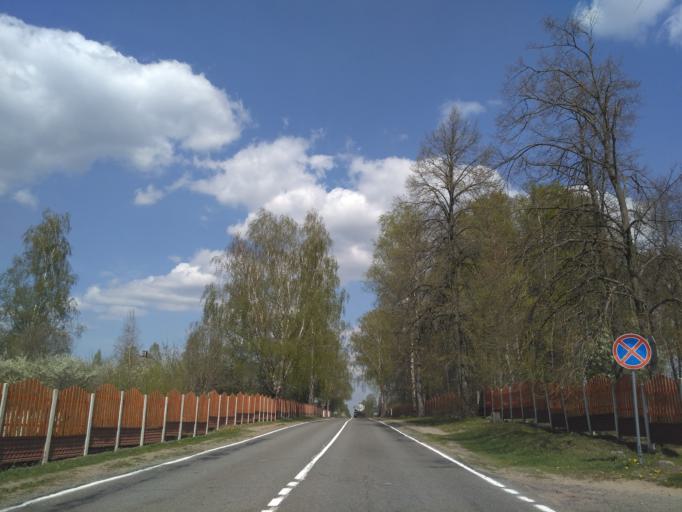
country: BY
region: Minsk
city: Myadzyel
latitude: 54.6934
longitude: 26.9253
